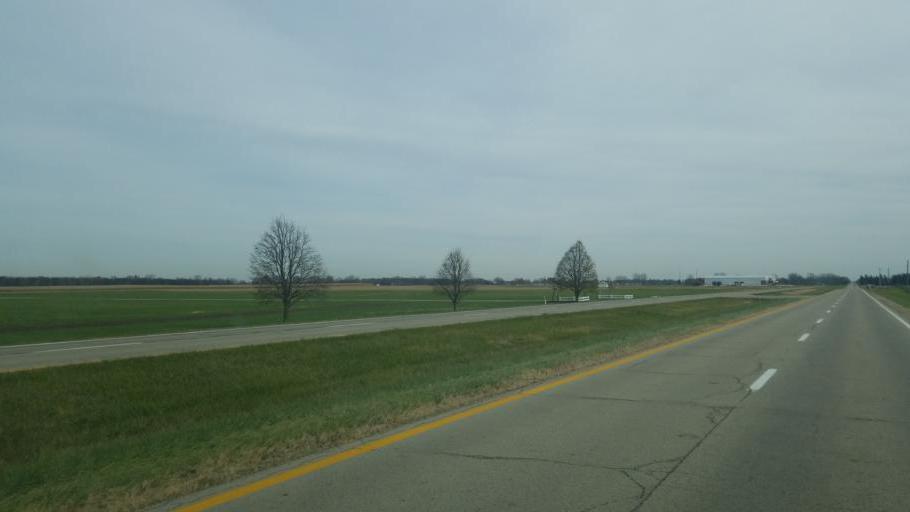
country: US
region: Ohio
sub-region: Madison County
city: London
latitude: 39.9364
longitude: -83.4348
